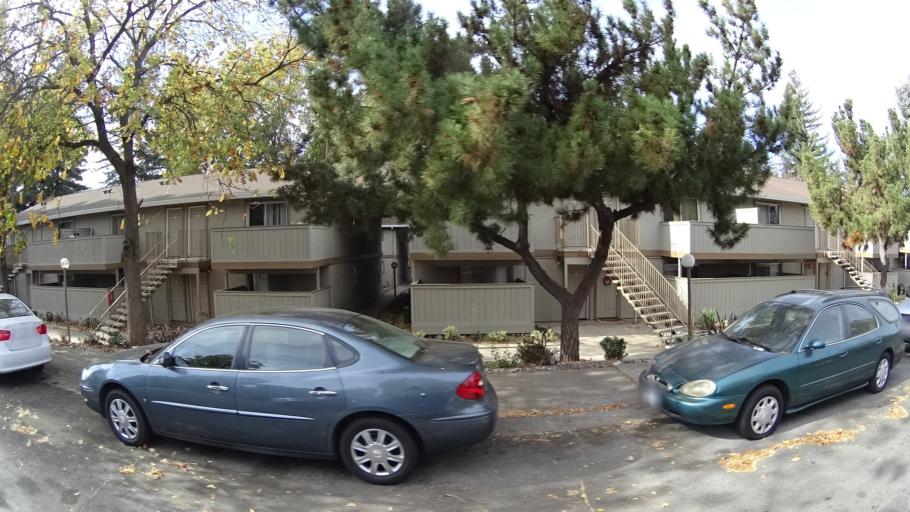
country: US
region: California
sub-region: Sacramento County
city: Fair Oaks
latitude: 38.6734
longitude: -121.2646
